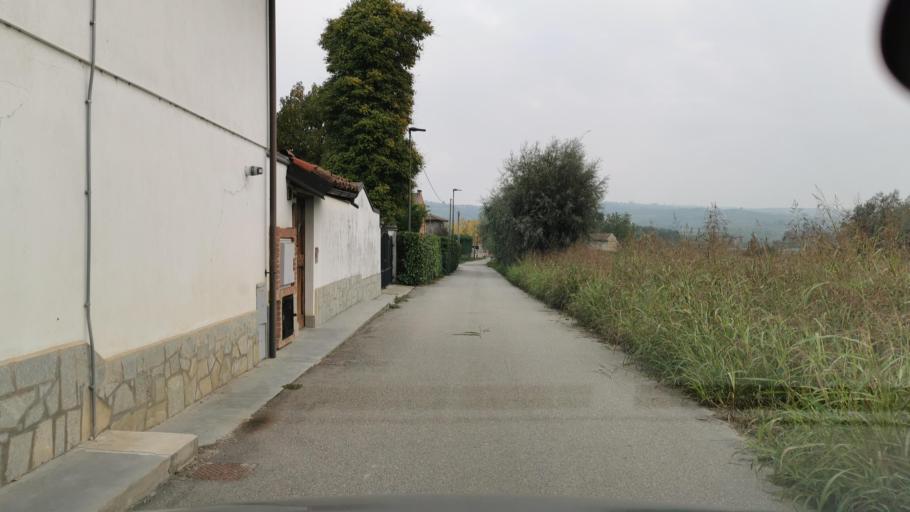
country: IT
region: Piedmont
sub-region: Provincia di Cuneo
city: Cinzano
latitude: 44.6932
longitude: 7.9116
